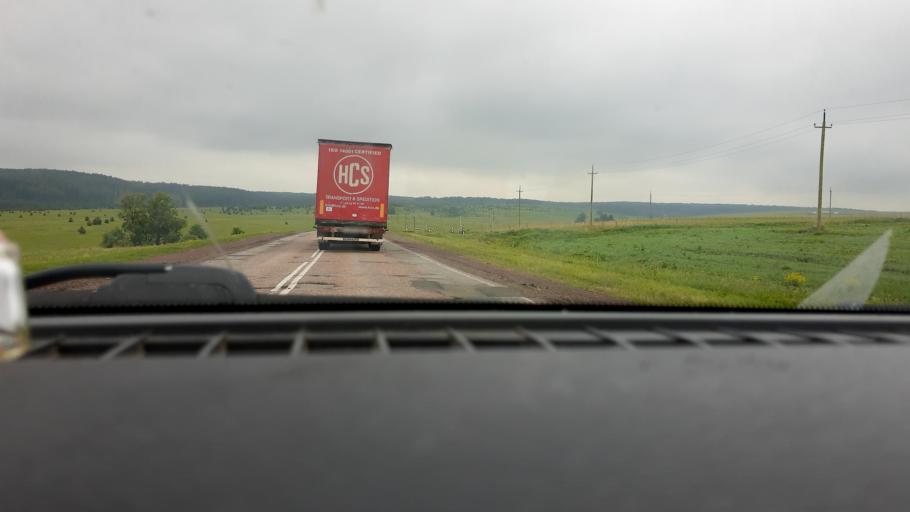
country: RU
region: Bashkortostan
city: Belebey
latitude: 54.2449
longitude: 54.0714
